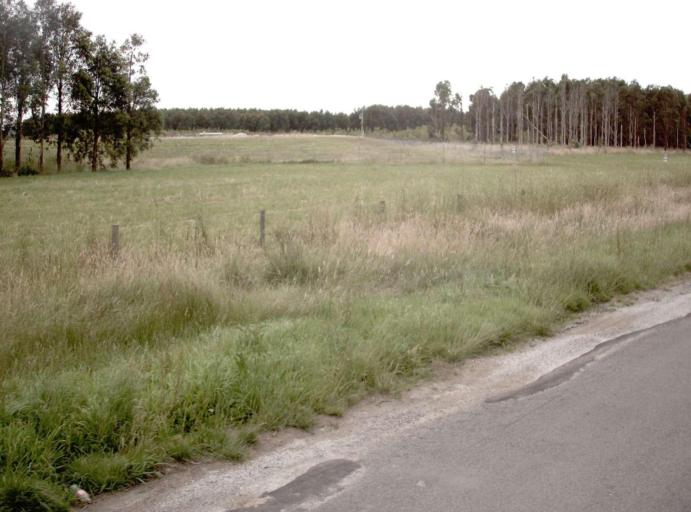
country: AU
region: Victoria
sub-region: Cardinia
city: Koo-Wee-Rup
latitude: -38.2726
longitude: 145.5479
